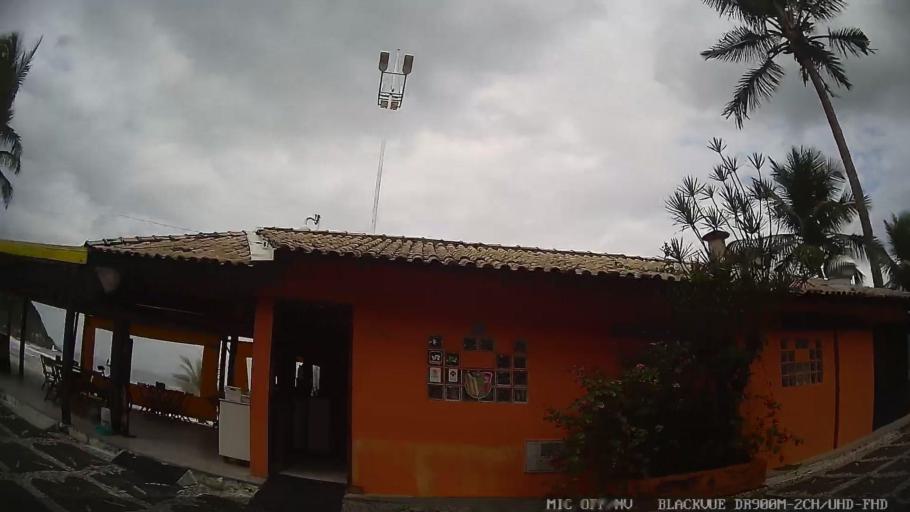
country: BR
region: Sao Paulo
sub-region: Guaruja
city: Guaruja
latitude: -24.0129
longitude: -46.2717
